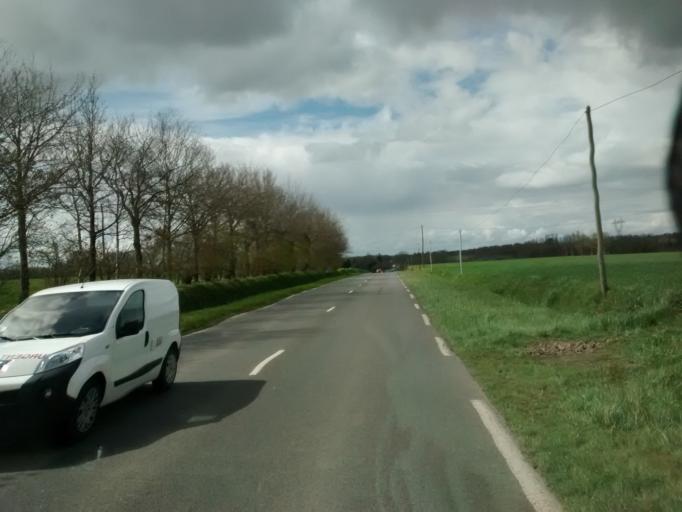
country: FR
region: Brittany
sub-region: Departement d'Ille-et-Vilaine
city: Chavagne
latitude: 48.0629
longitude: -1.8109
